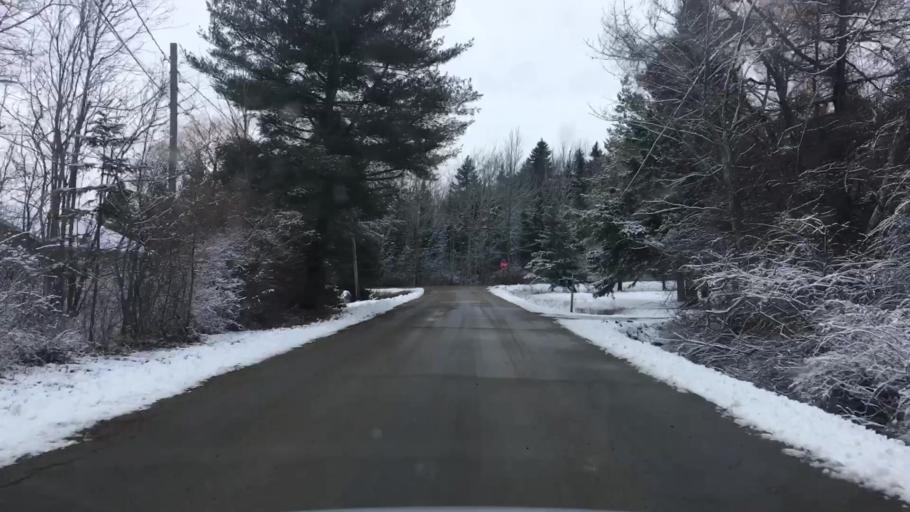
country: US
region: Maine
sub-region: Knox County
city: Owls Head
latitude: 44.0695
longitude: -69.0732
